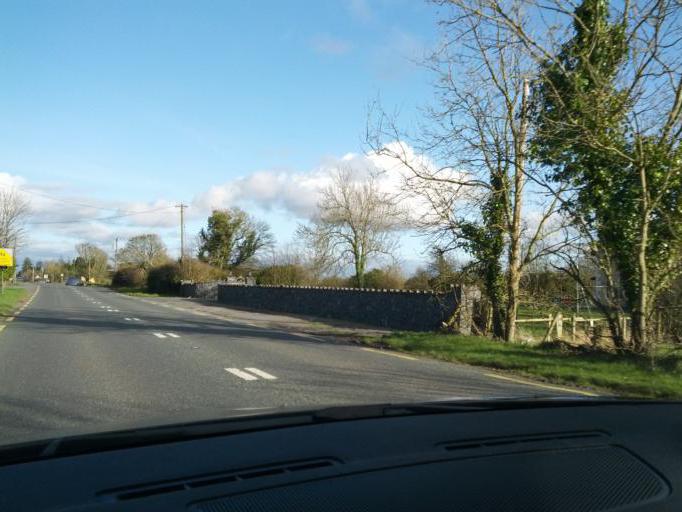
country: IE
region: Connaught
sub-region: Roscommon
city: Roscommon
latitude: 53.6532
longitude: -8.2545
